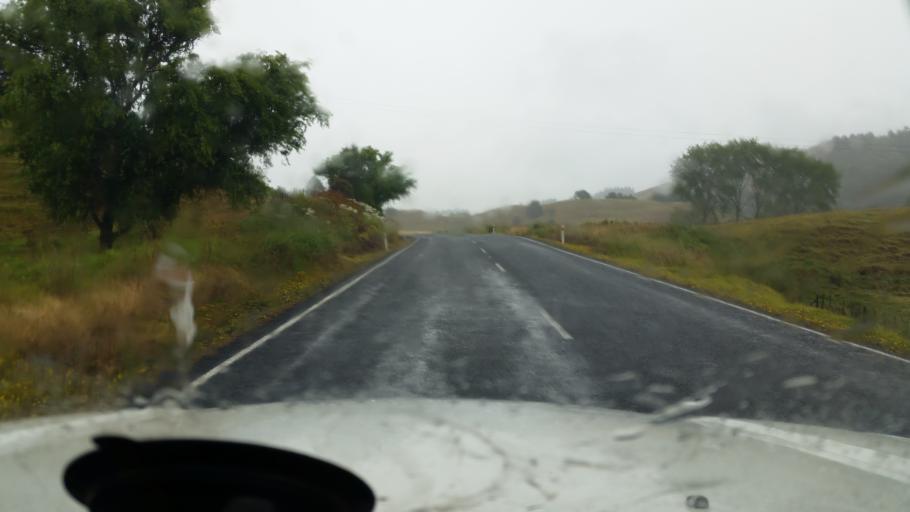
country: NZ
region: Northland
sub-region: Far North District
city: Kaitaia
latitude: -35.2731
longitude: 173.3549
